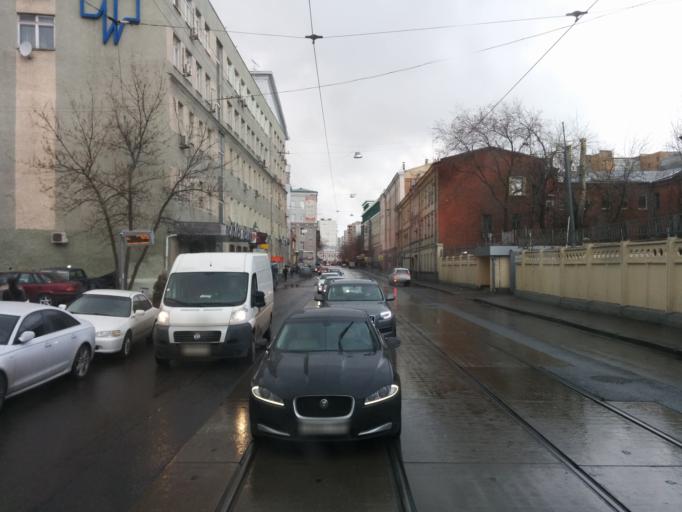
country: RU
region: Moscow
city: Mar'ina Roshcha
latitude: 55.7814
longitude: 37.6017
